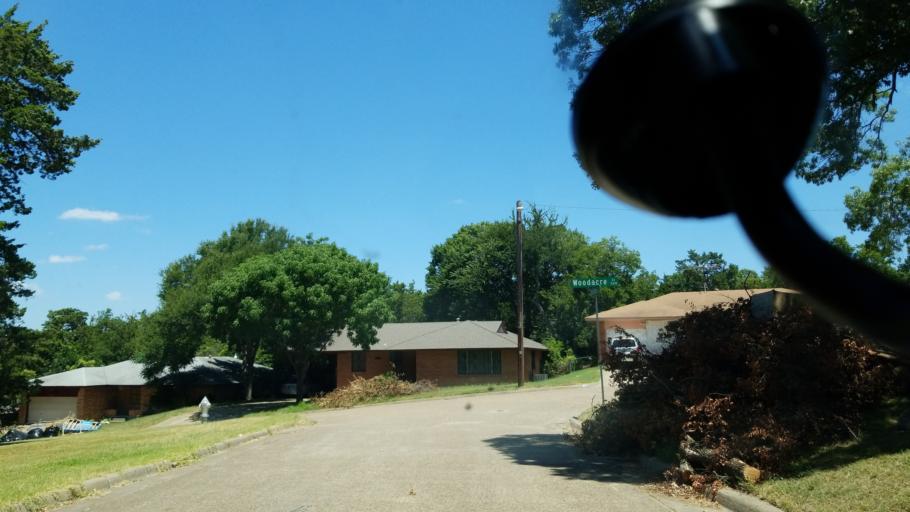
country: US
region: Texas
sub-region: Dallas County
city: Cockrell Hill
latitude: 32.6826
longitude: -96.8182
